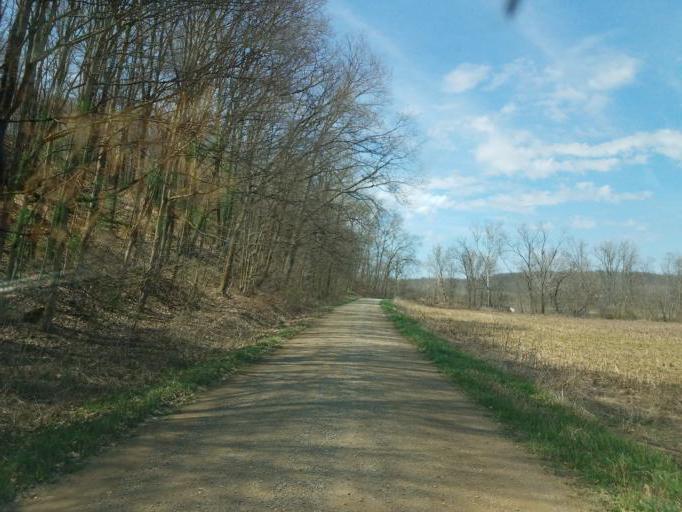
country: US
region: Ohio
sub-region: Knox County
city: Oak Hill
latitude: 40.3772
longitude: -82.2347
